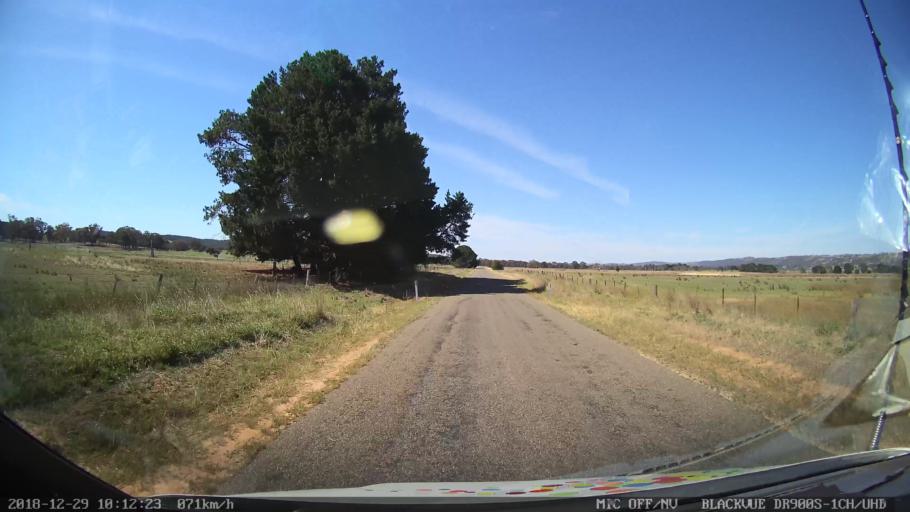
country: AU
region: New South Wales
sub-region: Yass Valley
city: Gundaroo
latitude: -34.8933
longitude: 149.4487
